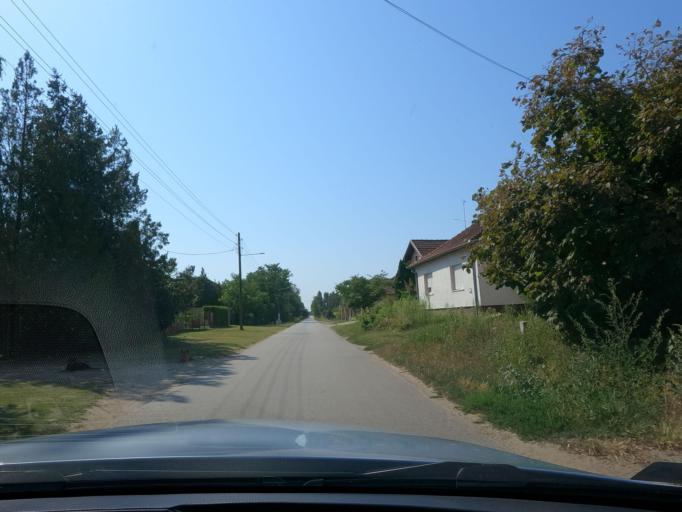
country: HU
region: Csongrad
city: Asotthalom
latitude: 46.0957
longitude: 19.7800
